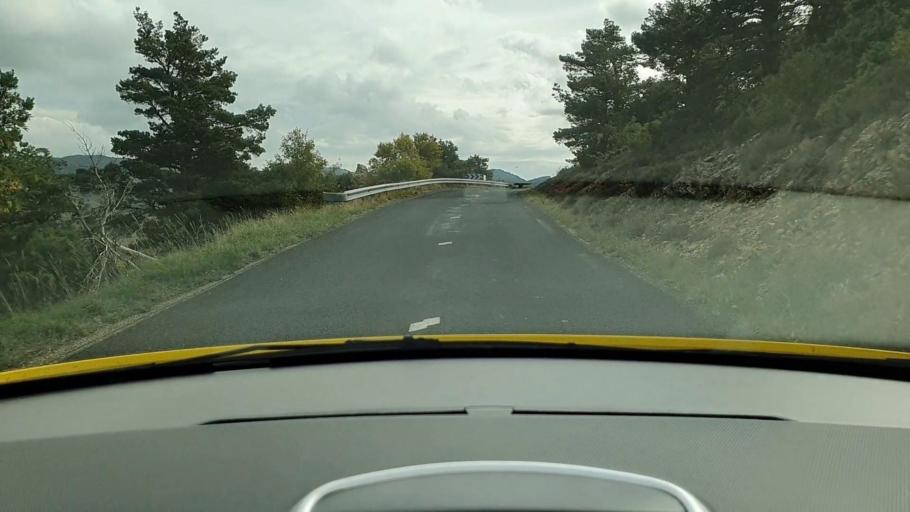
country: FR
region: Languedoc-Roussillon
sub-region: Departement de la Lozere
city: Meyrueis
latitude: 44.0660
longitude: 3.4119
